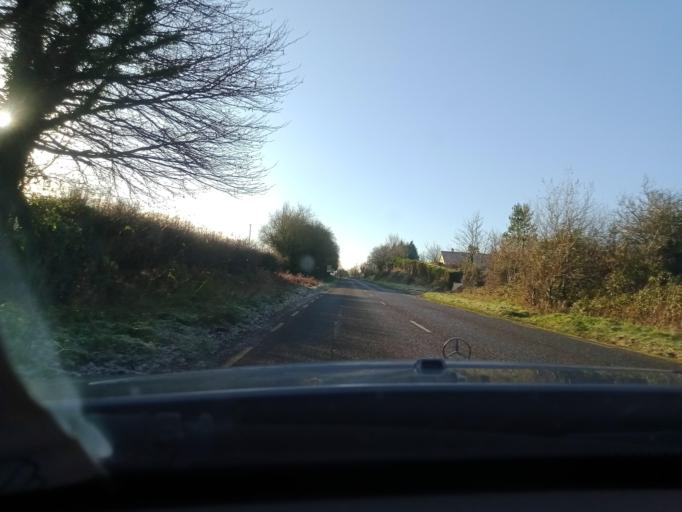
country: IE
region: Leinster
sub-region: Kilkenny
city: Graiguenamanagh
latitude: 52.5812
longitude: -6.9494
